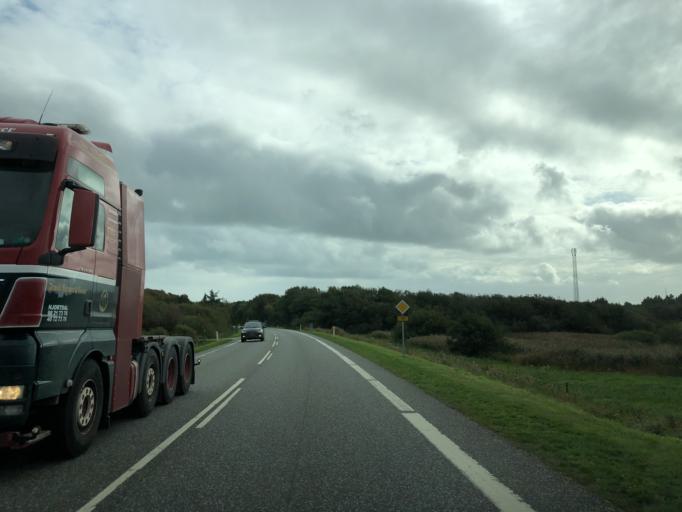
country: DK
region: North Denmark
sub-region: Thisted Kommune
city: Hurup
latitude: 56.6809
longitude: 8.3950
